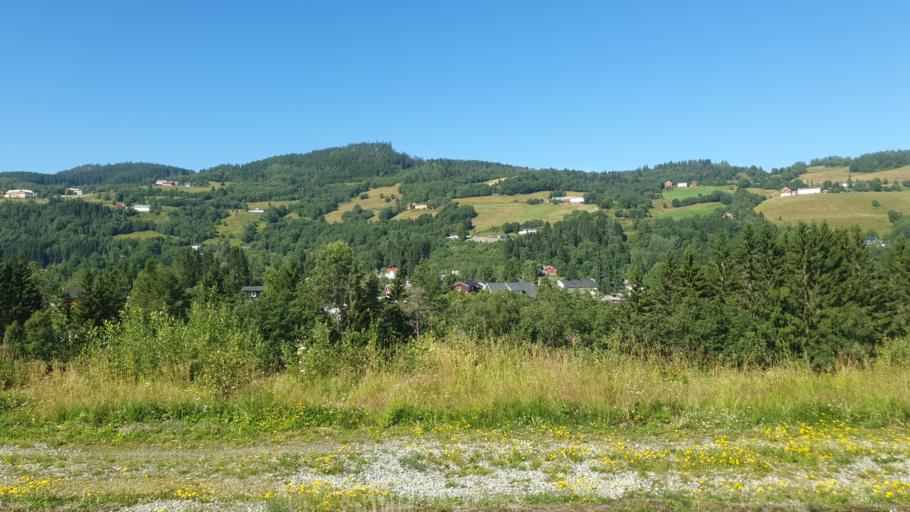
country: NO
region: Sor-Trondelag
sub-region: Meldal
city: Meldal
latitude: 63.1687
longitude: 9.7472
